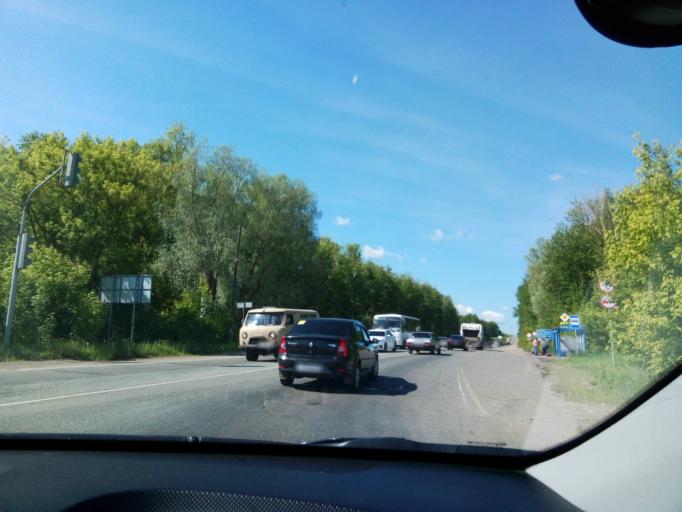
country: RU
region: Chuvashia
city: Novocheboksarsk
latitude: 56.0813
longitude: 47.5059
